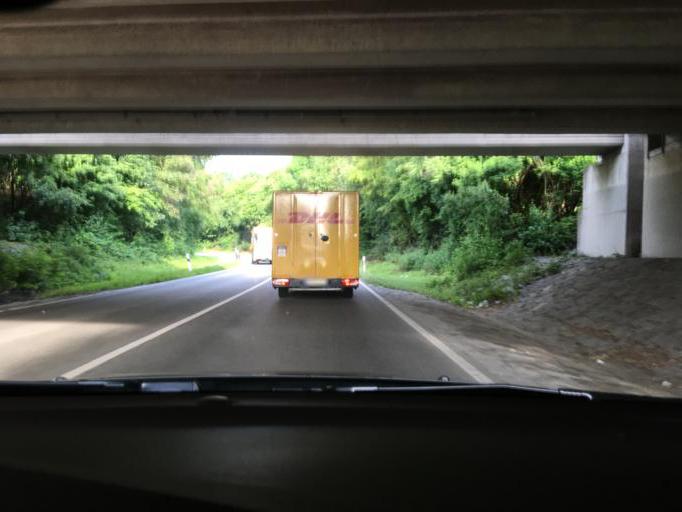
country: DE
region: Bavaria
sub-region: Upper Bavaria
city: Unterfoehring
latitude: 48.1762
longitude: 11.6377
